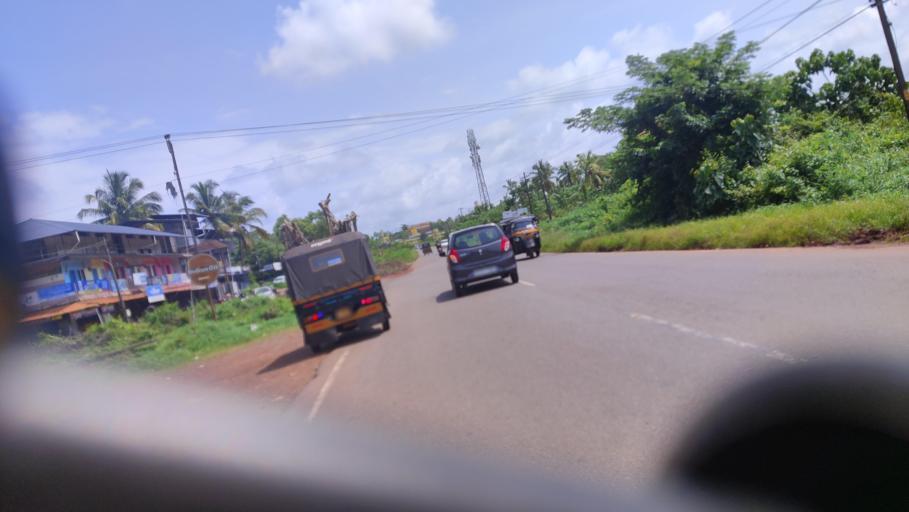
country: IN
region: Kerala
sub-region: Kasaragod District
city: Kannangad
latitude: 12.4037
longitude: 75.0965
